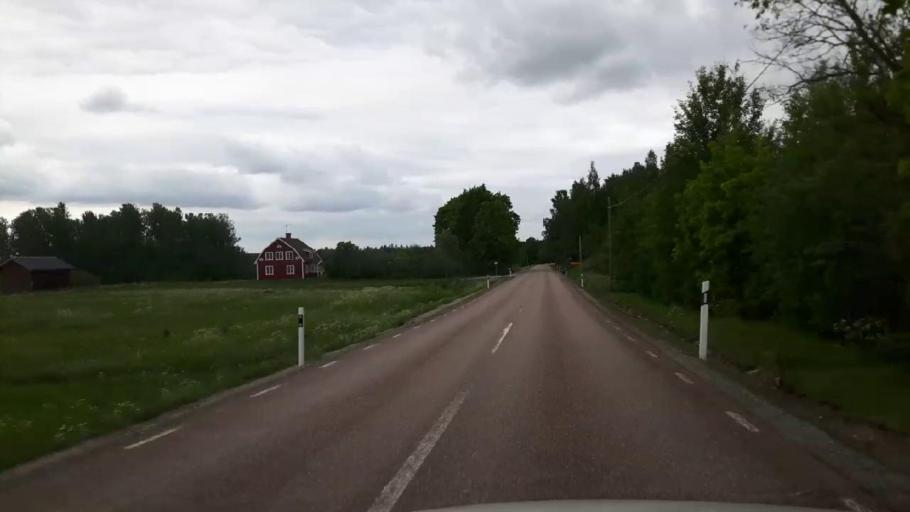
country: SE
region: Vaestmanland
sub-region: Kopings Kommun
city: Kolsva
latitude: 59.6893
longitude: 15.7744
